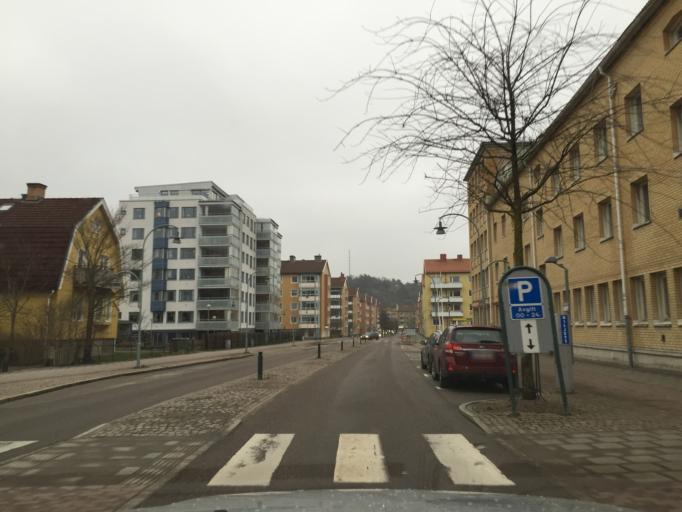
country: SE
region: Vaestra Goetaland
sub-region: Uddevalla Kommun
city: Uddevalla
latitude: 58.3527
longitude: 11.9267
